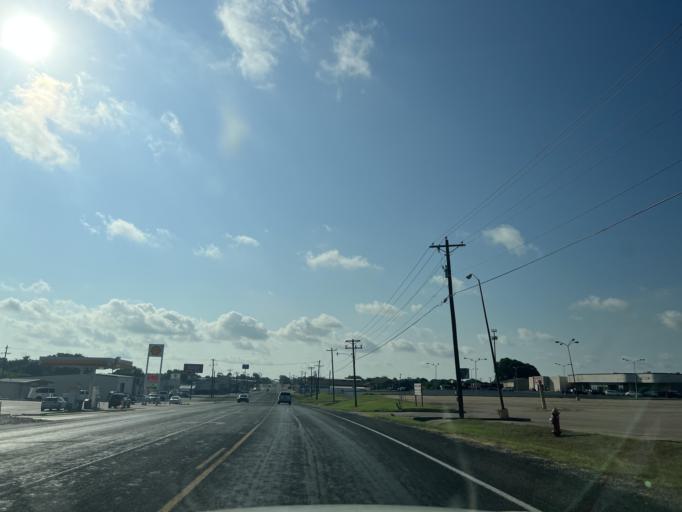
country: US
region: Texas
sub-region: Washington County
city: Brenham
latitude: 30.1505
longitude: -96.3896
